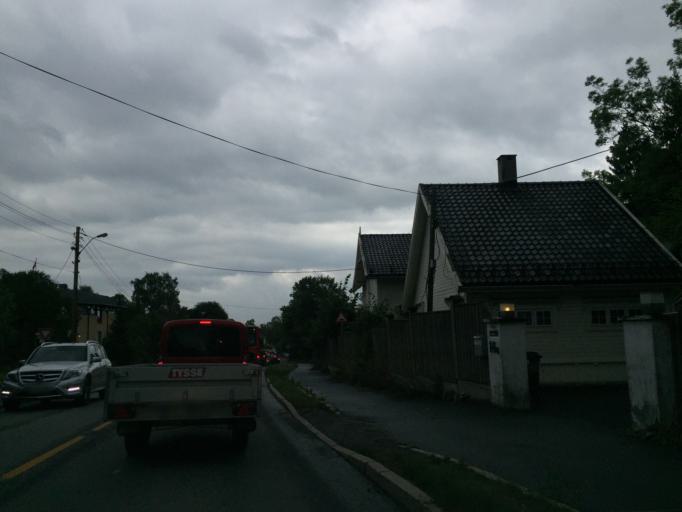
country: NO
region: Oslo
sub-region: Oslo
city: Sjolyststranda
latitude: 59.9425
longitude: 10.6815
